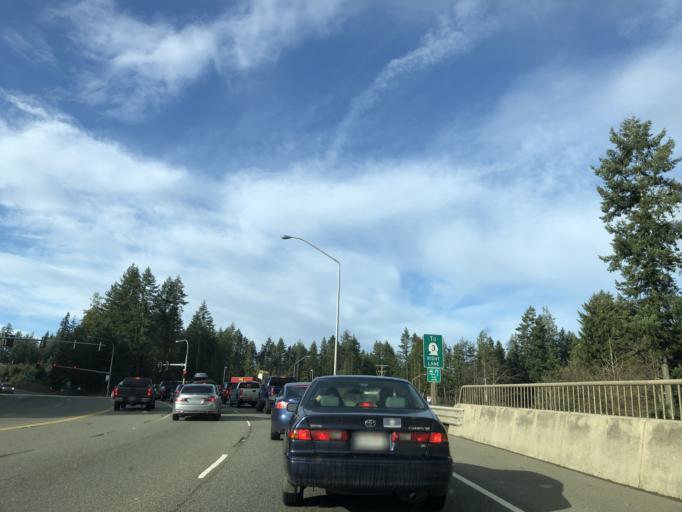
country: US
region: Washington
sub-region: Kitsap County
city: Poulsbo
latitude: 47.7567
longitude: -122.6513
